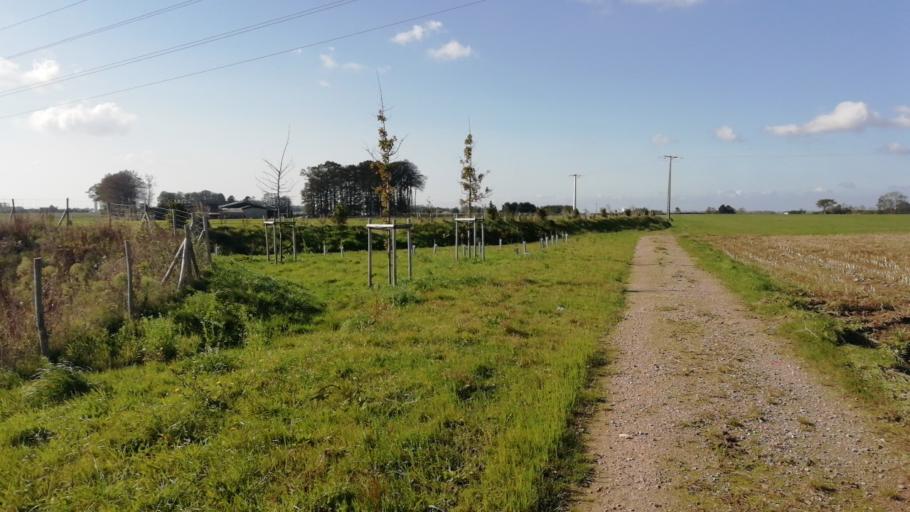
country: FR
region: Haute-Normandie
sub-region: Departement de la Seine-Maritime
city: Maneglise
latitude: 49.5911
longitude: 0.2735
